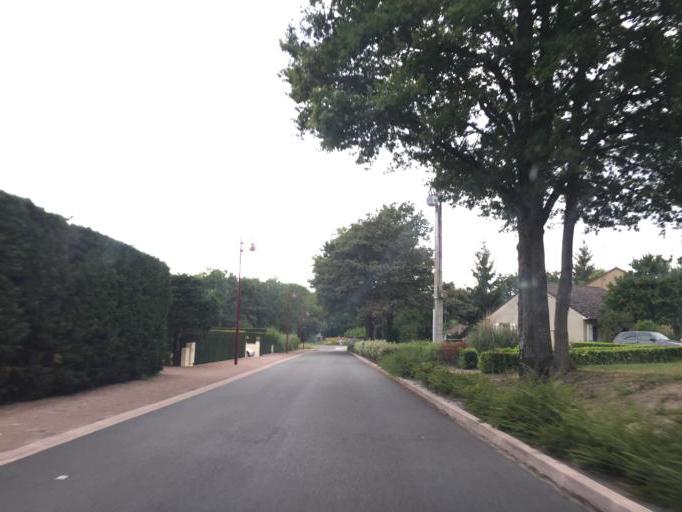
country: FR
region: Auvergne
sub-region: Departement de l'Allier
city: Lusigny
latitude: 46.5285
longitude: 3.4836
